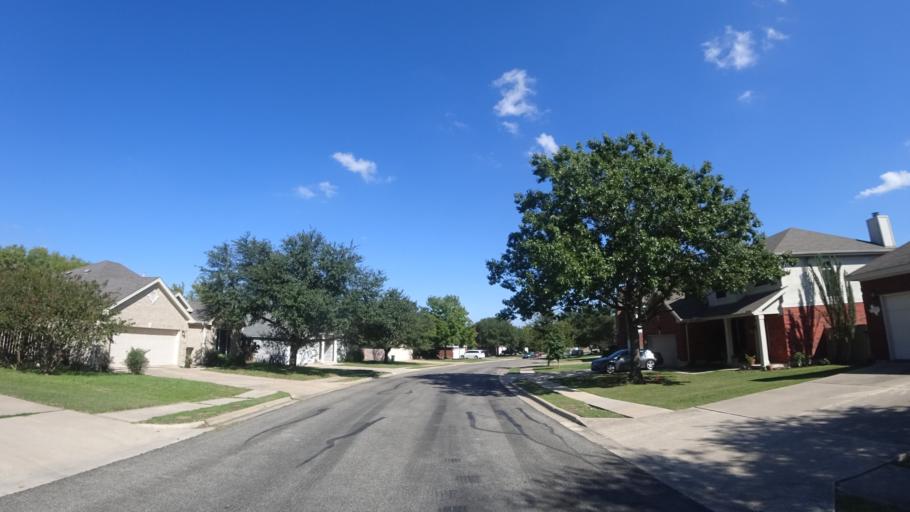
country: US
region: Texas
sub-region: Travis County
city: Manor
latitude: 30.3449
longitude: -97.6116
